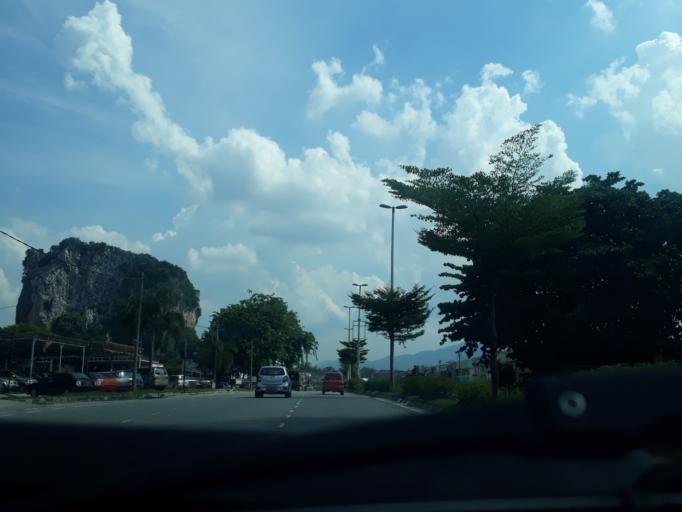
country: MY
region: Perak
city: Ipoh
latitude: 4.6444
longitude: 101.0983
